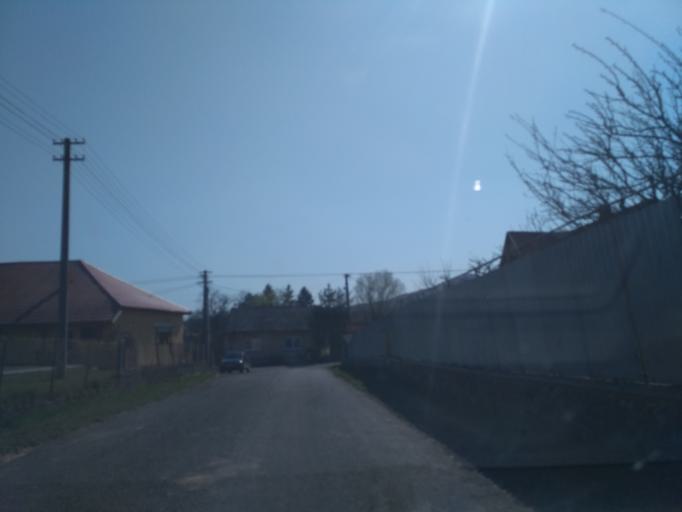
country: SK
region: Presovsky
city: Vranov nad Topl'ou
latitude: 48.8055
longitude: 21.6398
